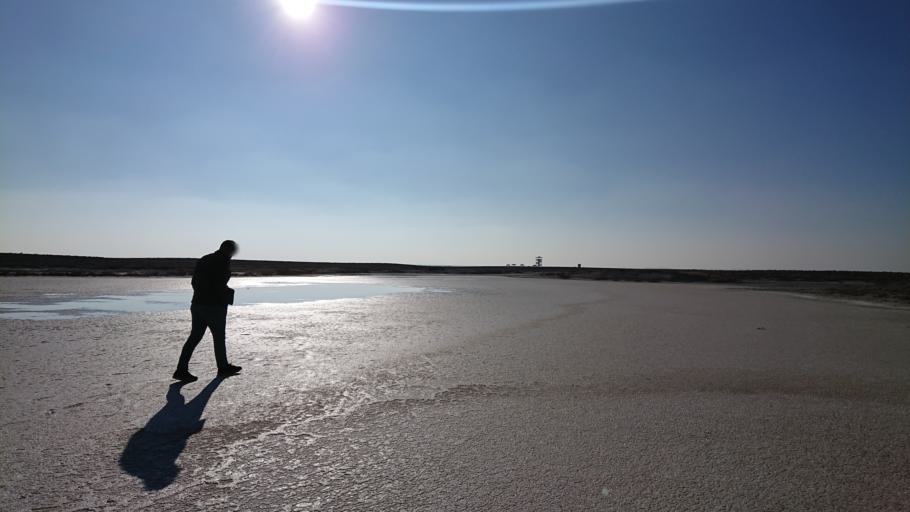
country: TR
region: Aksaray
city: Eskil
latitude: 38.4283
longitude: 33.5063
